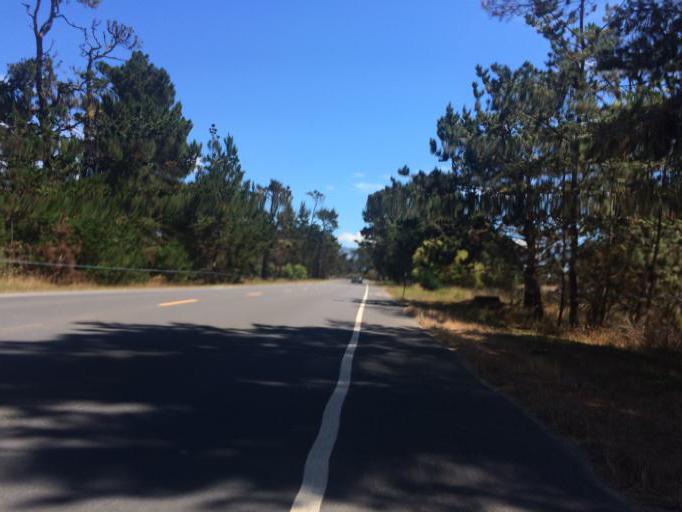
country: US
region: California
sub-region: Monterey County
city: Del Monte Forest
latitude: 36.5764
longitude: -121.9542
